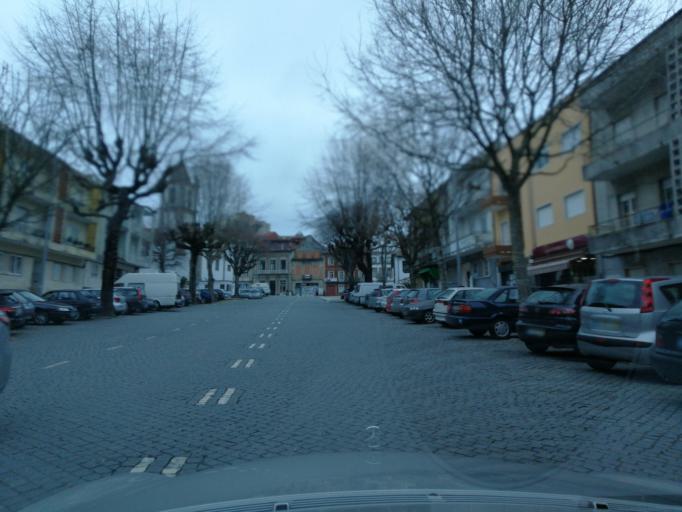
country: PT
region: Braga
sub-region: Braga
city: Braga
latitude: 41.5512
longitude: -8.4149
